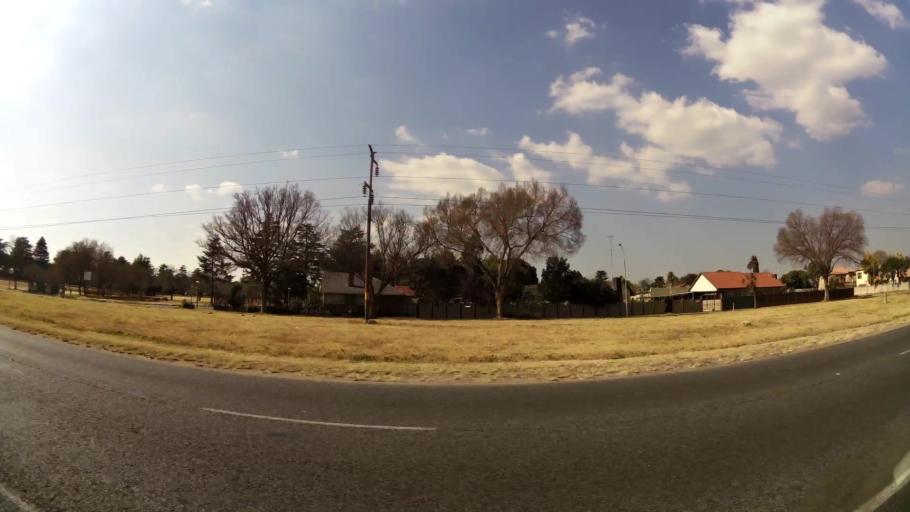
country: ZA
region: Gauteng
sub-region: City of Johannesburg Metropolitan Municipality
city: Modderfontein
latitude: -26.0871
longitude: 28.2220
